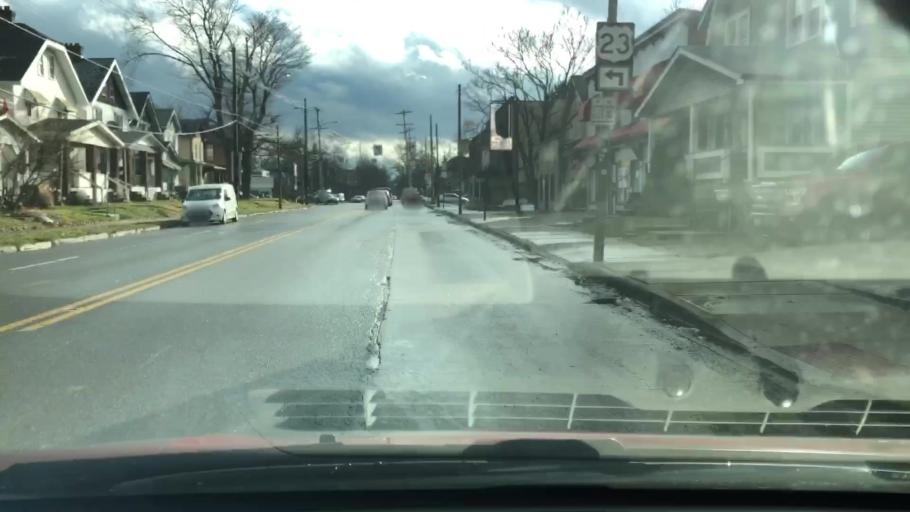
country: US
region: Ohio
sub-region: Franklin County
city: Grandview Heights
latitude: 40.0163
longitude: -83.0022
